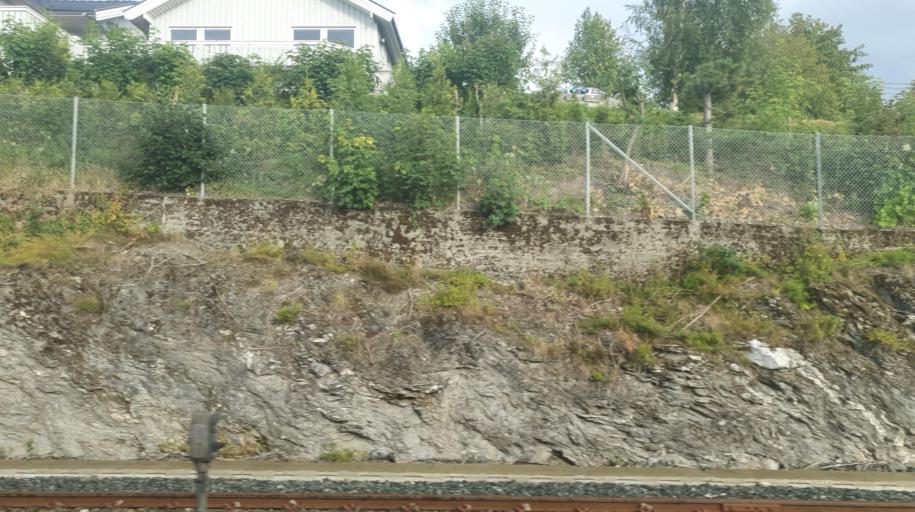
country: NO
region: Nord-Trondelag
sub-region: Levanger
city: Skogn
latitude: 63.7073
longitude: 11.1965
